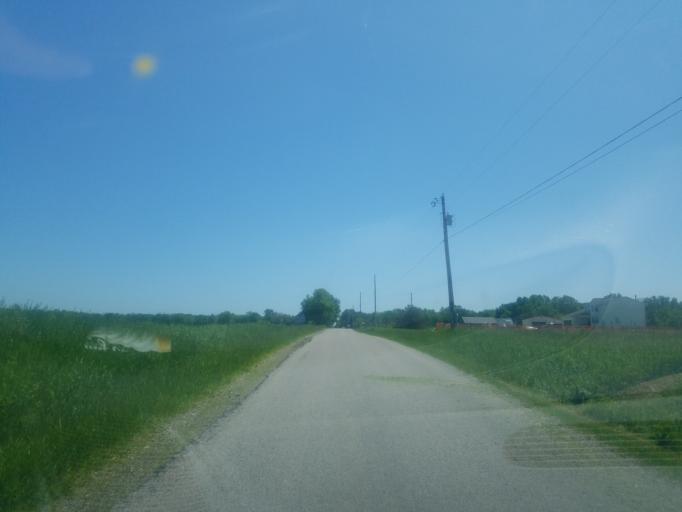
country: US
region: Ohio
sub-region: Huron County
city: New London
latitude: 41.1379
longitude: -82.3779
